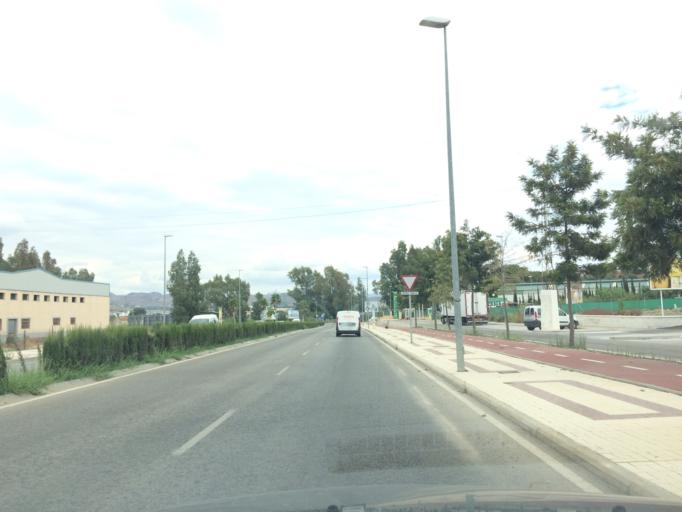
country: ES
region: Andalusia
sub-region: Provincia de Malaga
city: Estacion de Cartama
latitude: 36.7214
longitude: -4.6165
